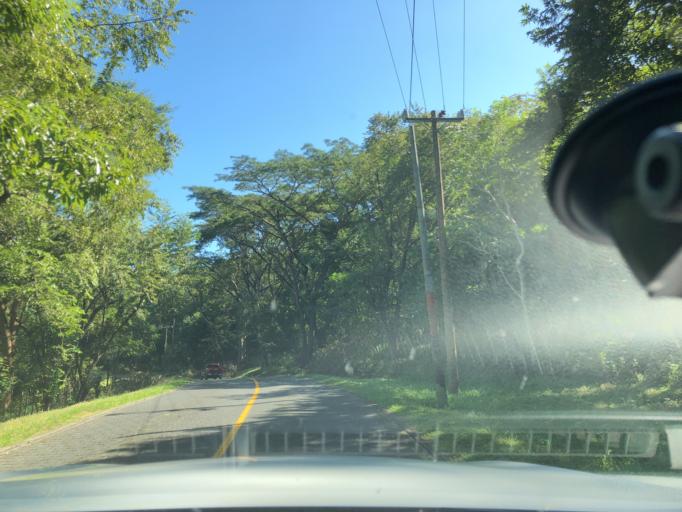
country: NI
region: Rivas
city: Cardenas
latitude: 11.2343
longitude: -85.5589
